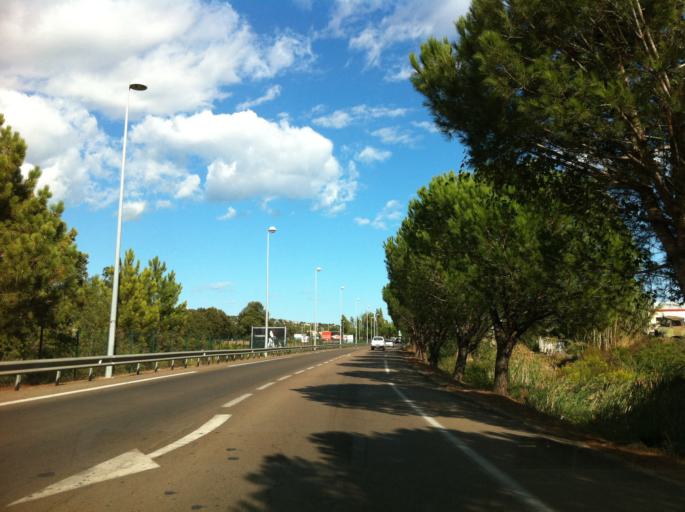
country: FR
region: Corsica
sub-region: Departement de la Corse-du-Sud
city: Porto-Vecchio
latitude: 41.6040
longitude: 9.2721
